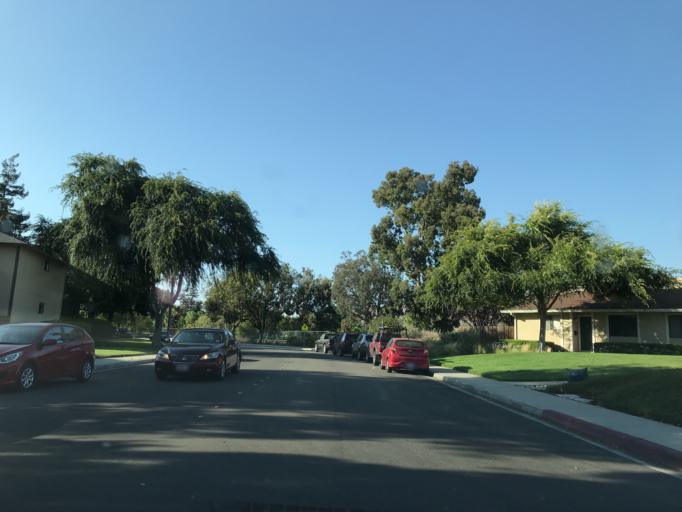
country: US
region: California
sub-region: Santa Clara County
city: Milpitas
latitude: 37.4410
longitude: -121.9151
